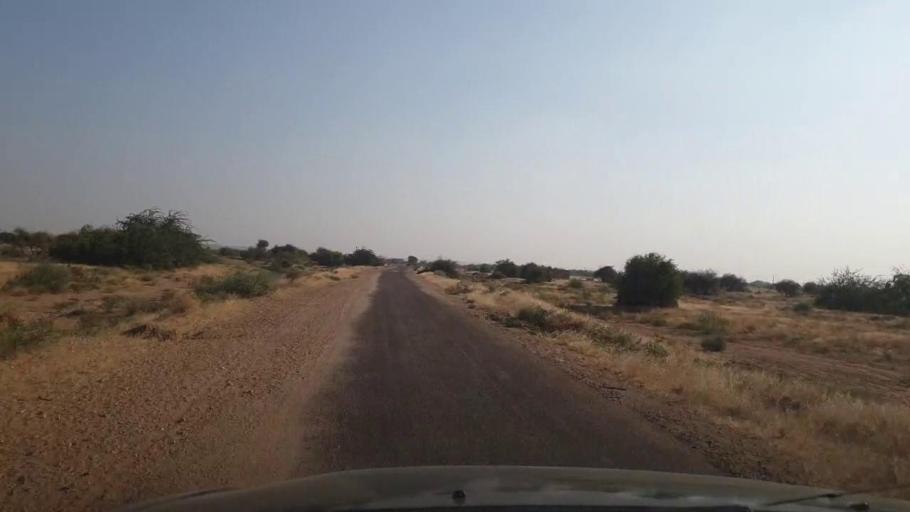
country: PK
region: Sindh
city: Jamshoro
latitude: 25.3449
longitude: 67.8387
